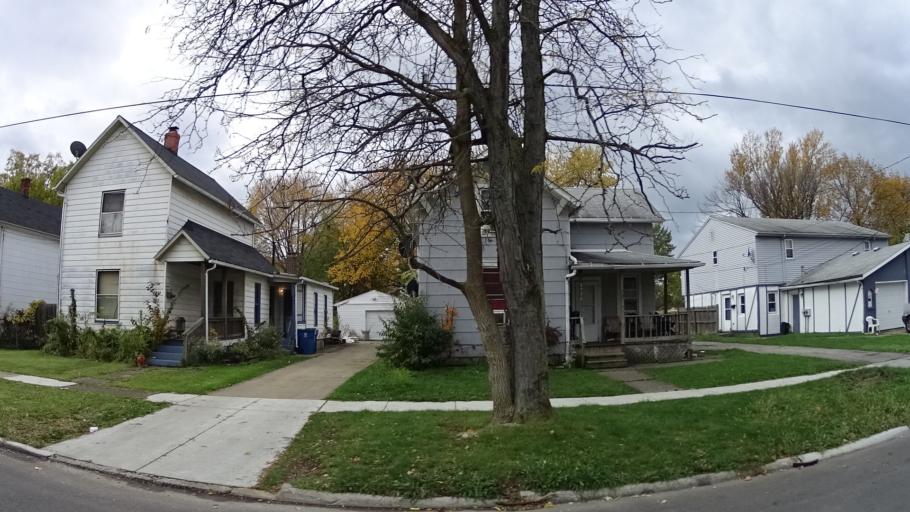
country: US
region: Ohio
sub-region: Lorain County
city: Lorain
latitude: 41.4548
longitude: -82.1708
